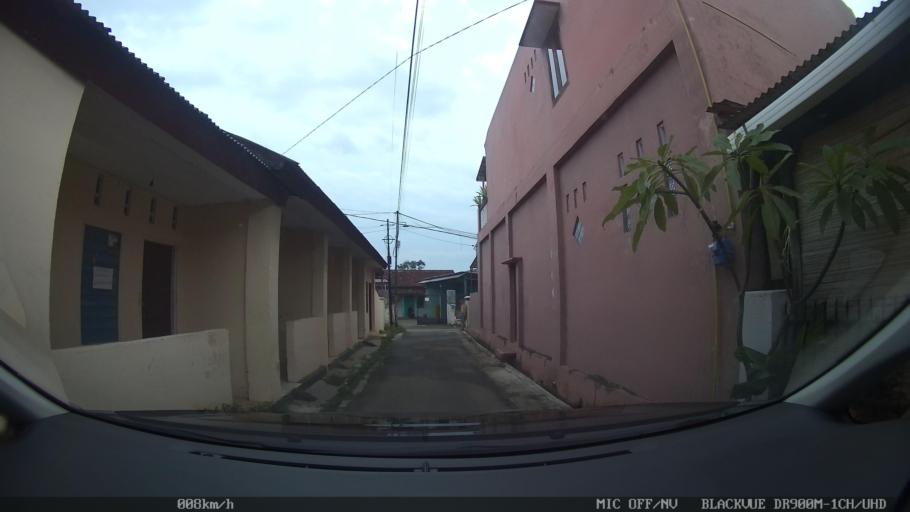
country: ID
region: Lampung
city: Kedaton
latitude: -5.3825
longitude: 105.2551
